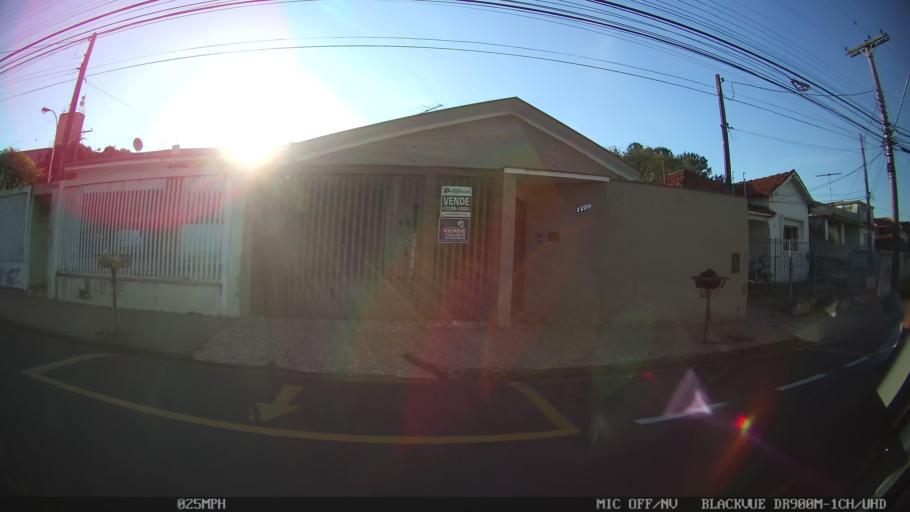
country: BR
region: Sao Paulo
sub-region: Sao Jose Do Rio Preto
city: Sao Jose do Rio Preto
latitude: -20.8013
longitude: -49.3672
